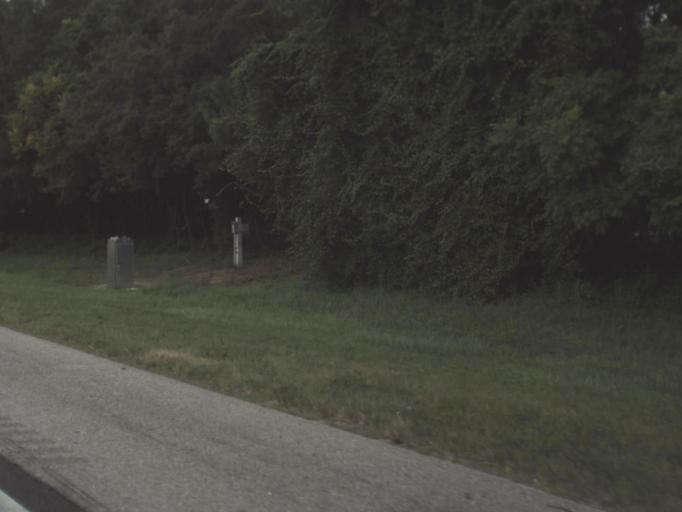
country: US
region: Florida
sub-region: Sarasota County
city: Fruitville
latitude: 27.3174
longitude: -82.4481
